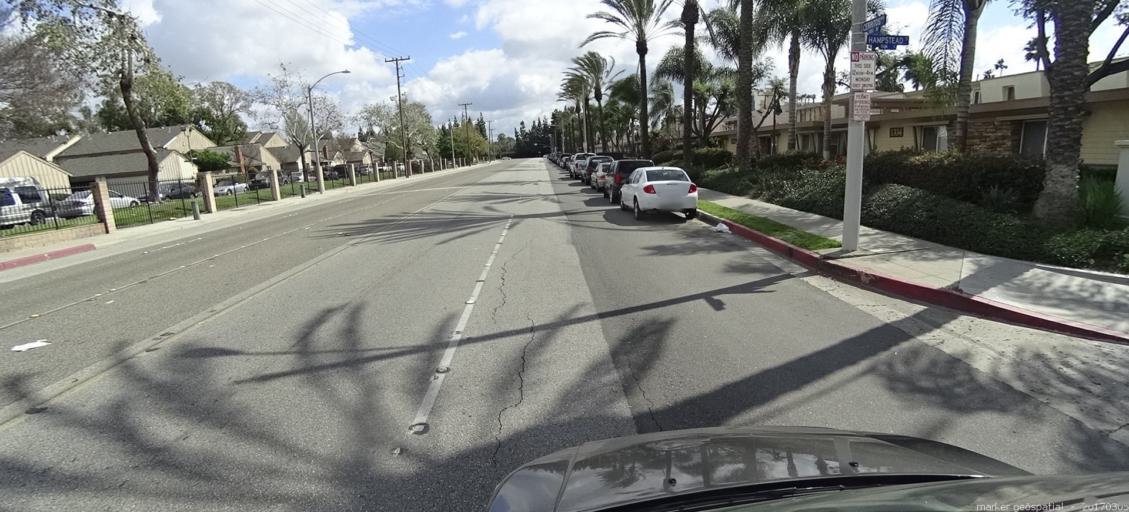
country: US
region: California
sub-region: Orange County
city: Anaheim
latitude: 33.8105
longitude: -117.9315
